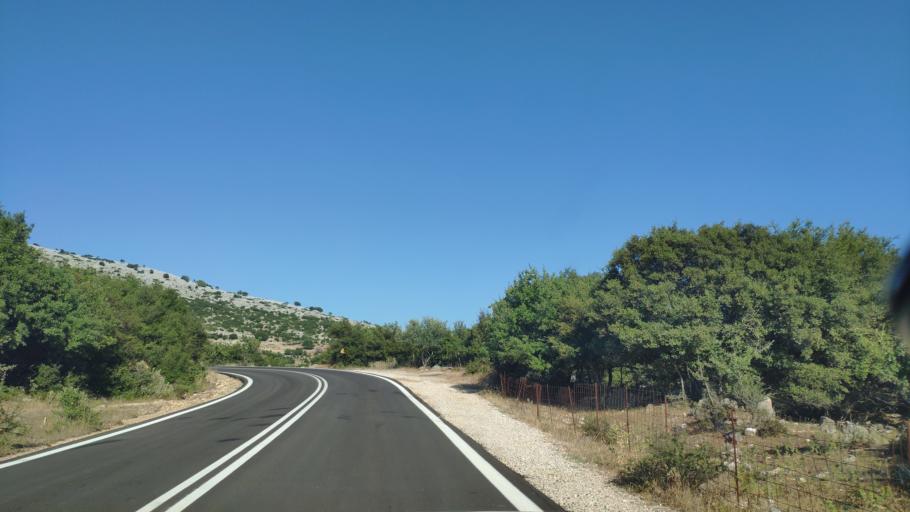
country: GR
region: West Greece
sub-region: Nomos Aitolias kai Akarnanias
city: Archontochorion
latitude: 38.6915
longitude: 21.0558
